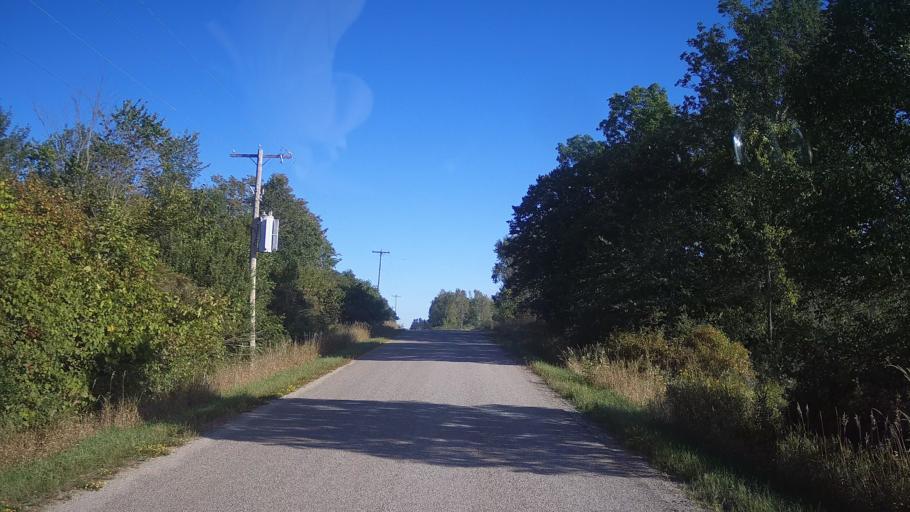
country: US
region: New York
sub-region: Jefferson County
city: Alexandria Bay
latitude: 44.4203
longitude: -75.9781
